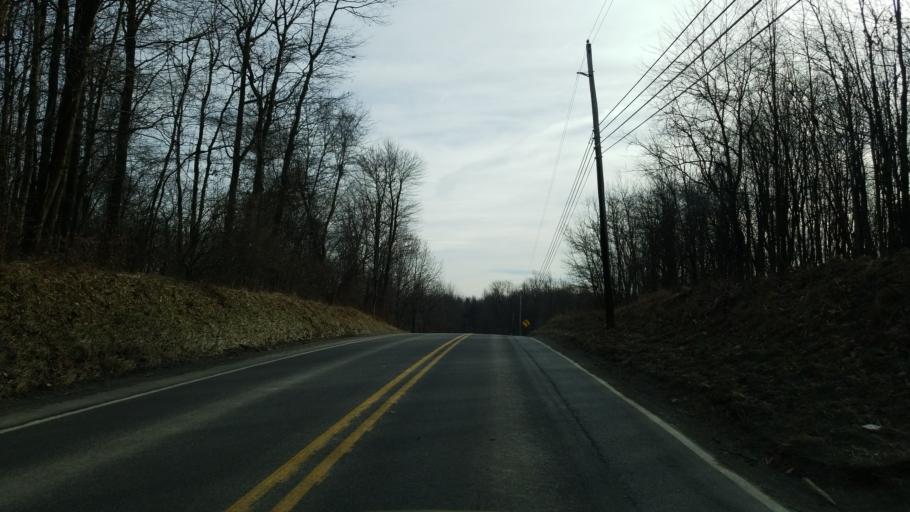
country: US
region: Pennsylvania
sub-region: Indiana County
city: Johnsonburg
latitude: 40.9180
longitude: -78.8468
